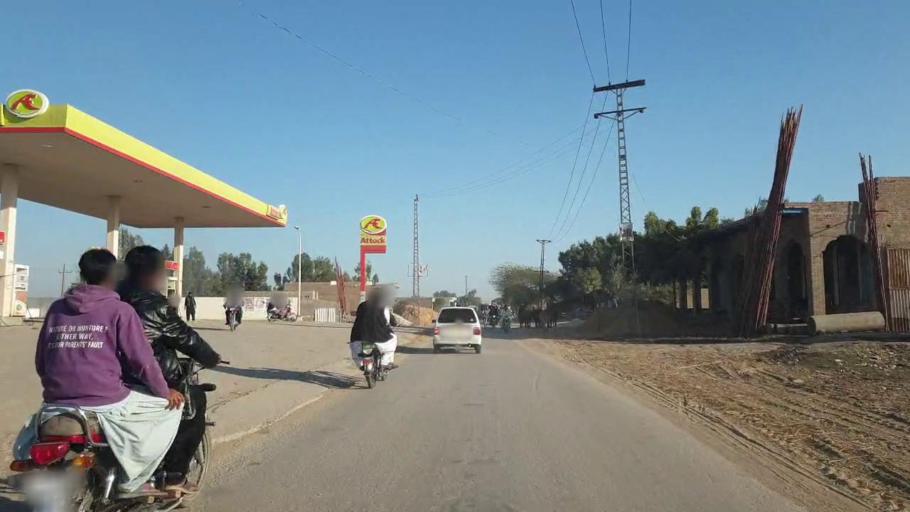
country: PK
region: Sindh
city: Dokri
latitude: 27.3679
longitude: 68.1098
